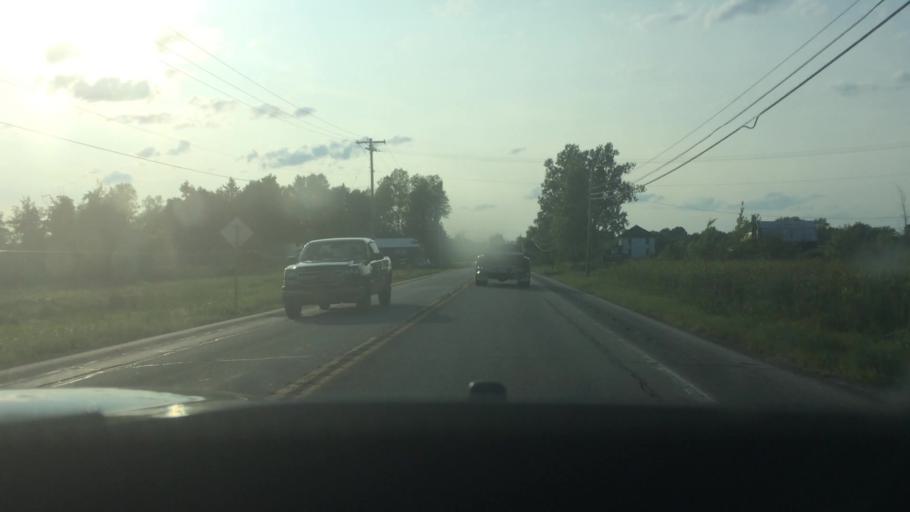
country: US
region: New York
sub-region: St. Lawrence County
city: Ogdensburg
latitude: 44.6868
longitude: -75.4542
